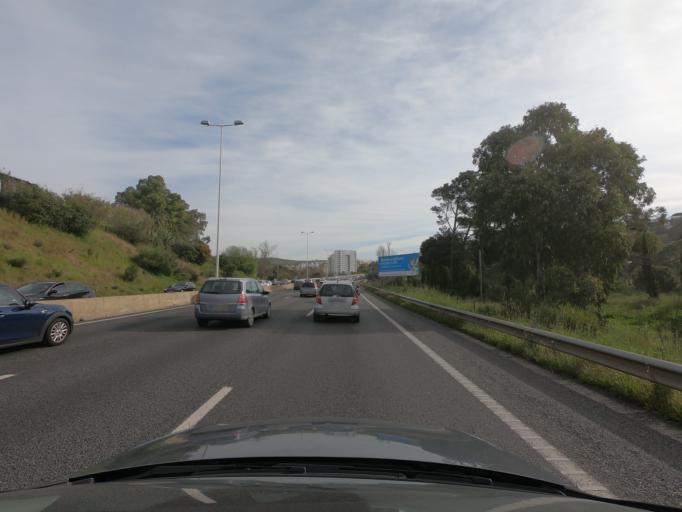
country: PT
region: Lisbon
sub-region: Oeiras
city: Linda-a-Velha
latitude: 38.7172
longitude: -9.2515
